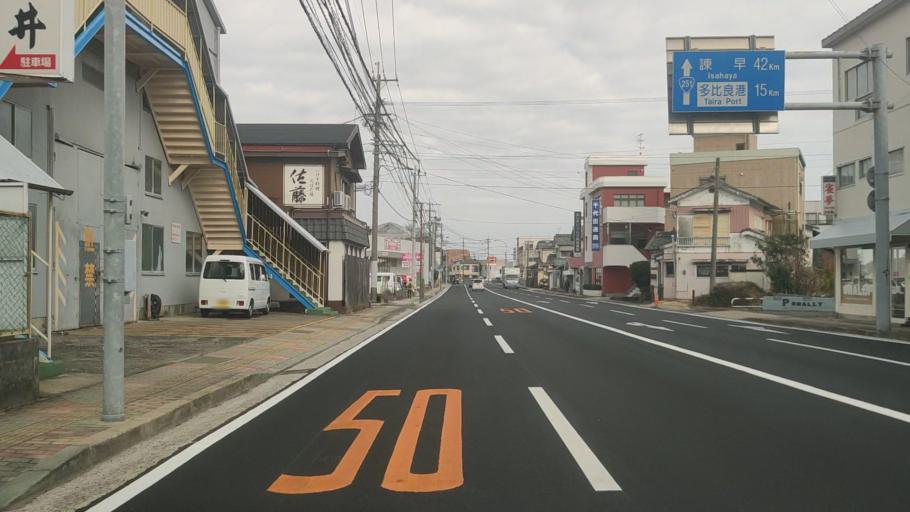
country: JP
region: Nagasaki
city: Shimabara
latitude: 32.7686
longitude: 130.3720
